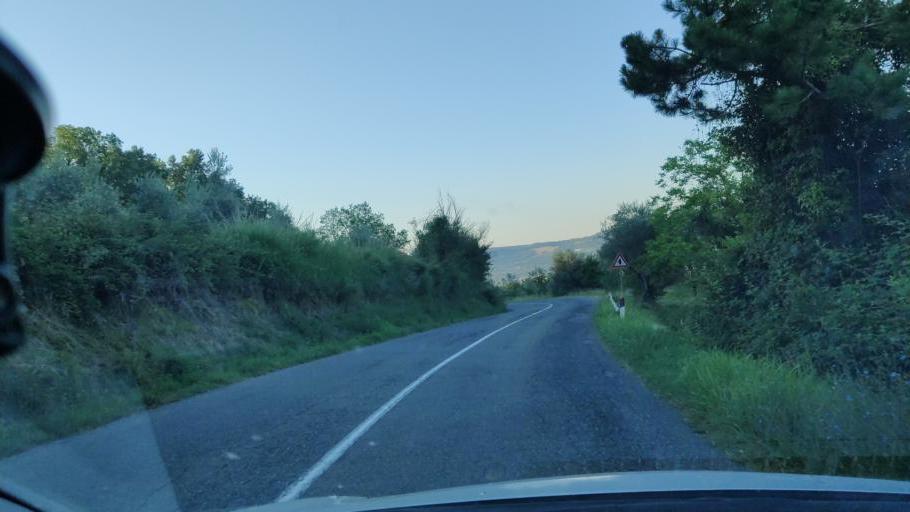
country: IT
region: Umbria
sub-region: Provincia di Terni
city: Giove
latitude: 42.5030
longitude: 12.3215
